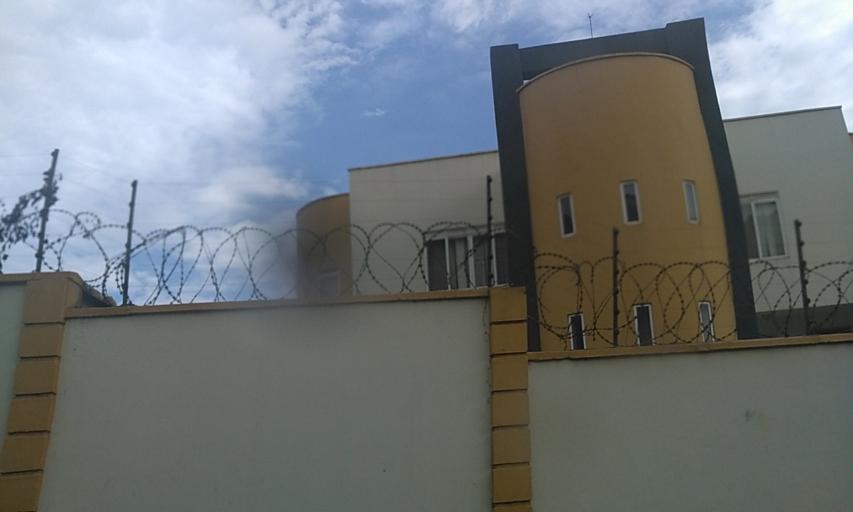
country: UG
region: Central Region
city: Kampala Central Division
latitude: 0.3372
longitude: 32.5924
